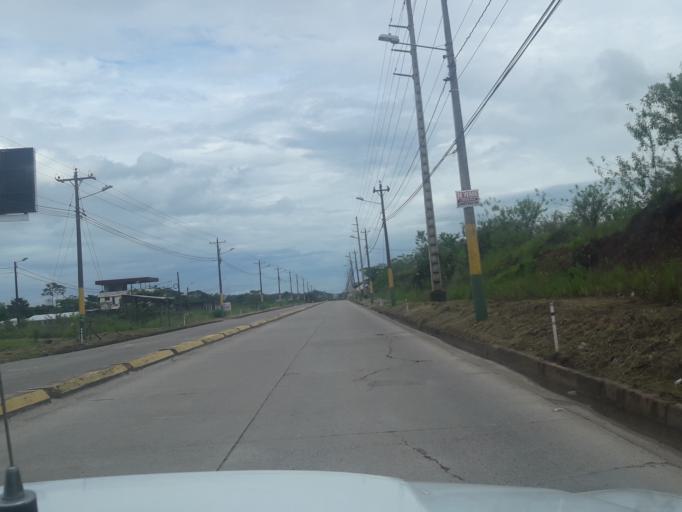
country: EC
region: Napo
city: Archidona
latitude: -0.9471
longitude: -77.8173
